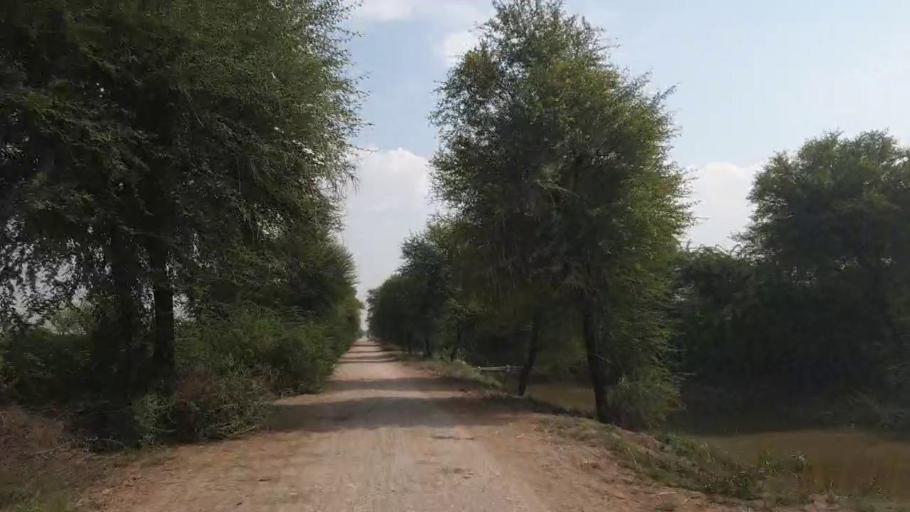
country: PK
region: Sindh
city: Tando Bago
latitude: 24.9292
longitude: 69.0093
